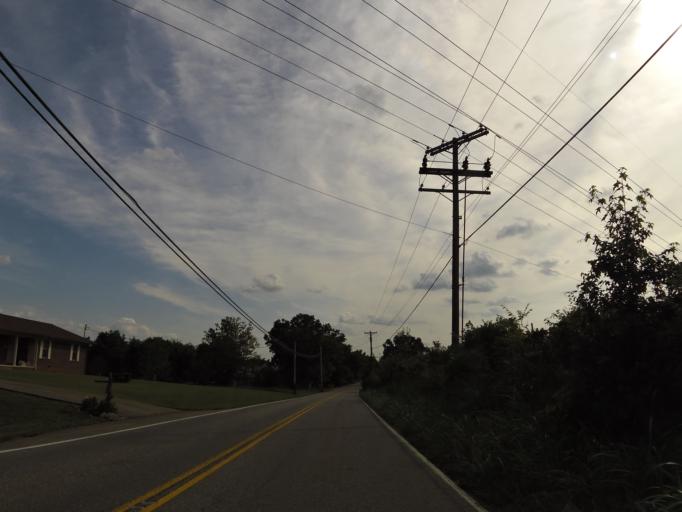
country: US
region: Tennessee
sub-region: Blount County
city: Wildwood
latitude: 35.8076
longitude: -83.8410
